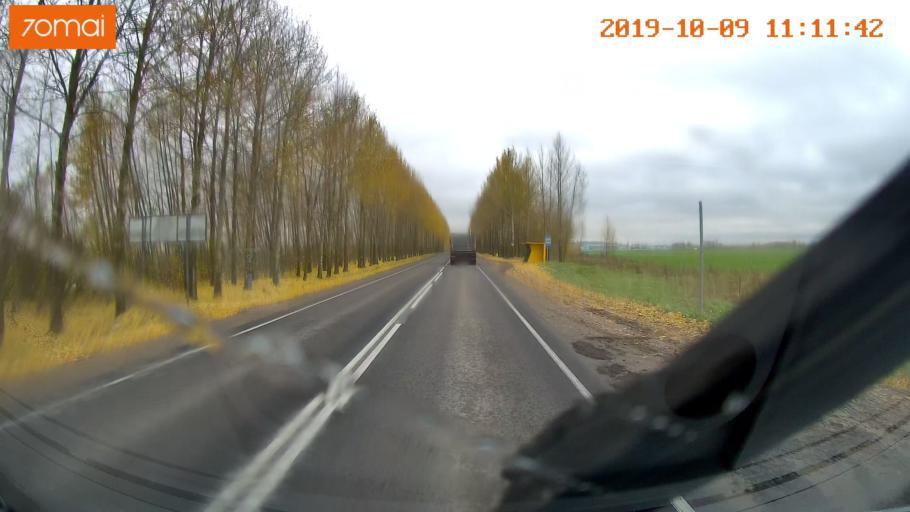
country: RU
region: Vologda
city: Vologda
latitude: 59.1707
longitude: 39.8231
